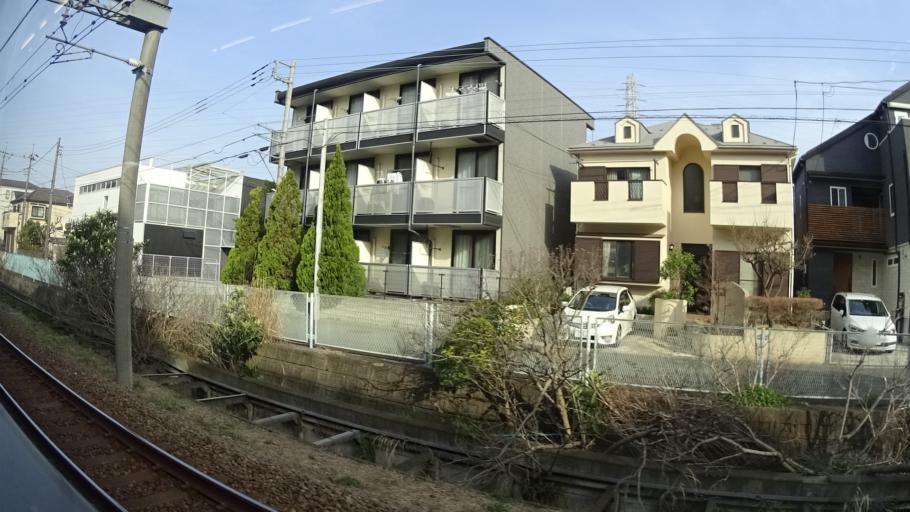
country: JP
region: Kanagawa
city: Minami-rinkan
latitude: 35.4607
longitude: 139.5213
